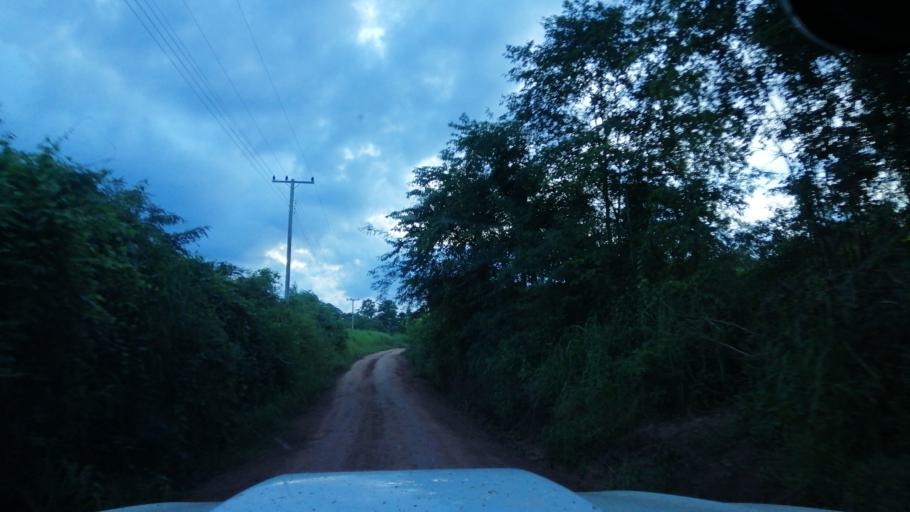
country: TH
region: Uttaradit
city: Ban Khok
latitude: 17.8763
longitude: 101.0765
